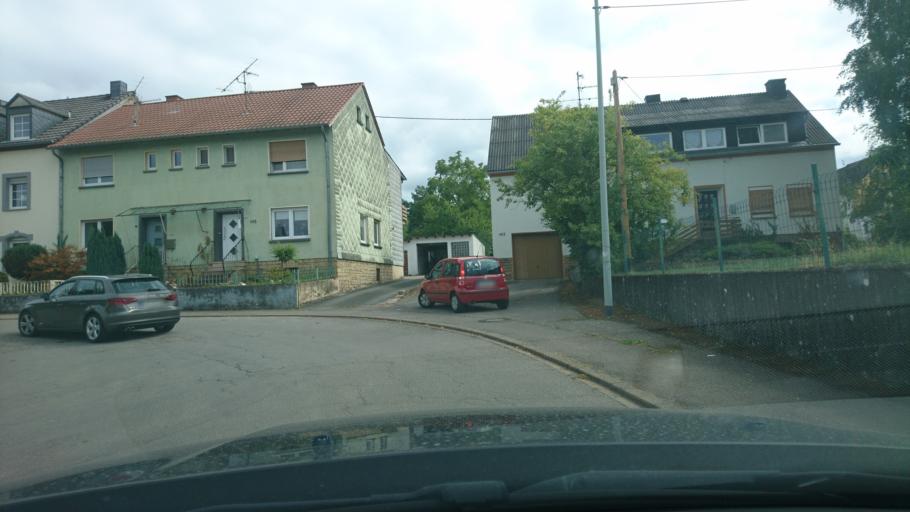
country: DE
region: Rheinland-Pfalz
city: Wiltingen
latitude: 49.6608
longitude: 6.5902
